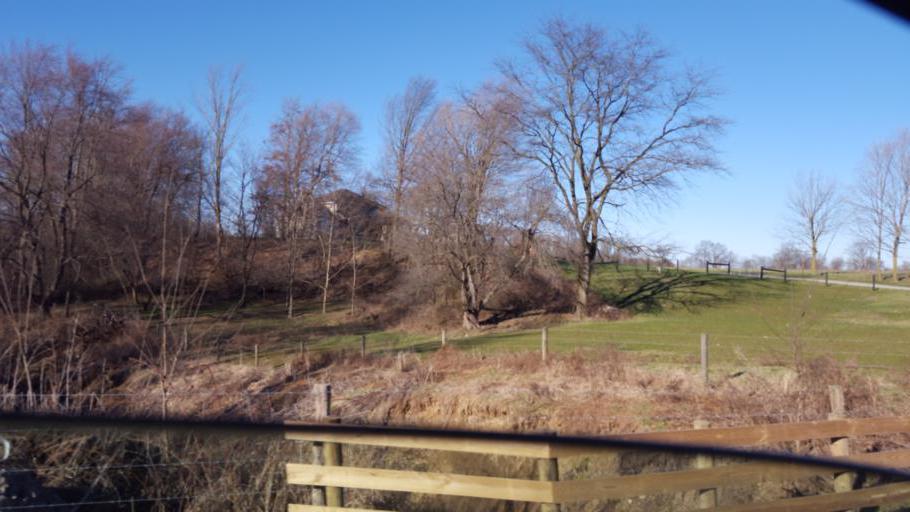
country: US
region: Ohio
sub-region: Holmes County
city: Millersburg
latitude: 40.5986
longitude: -81.7746
